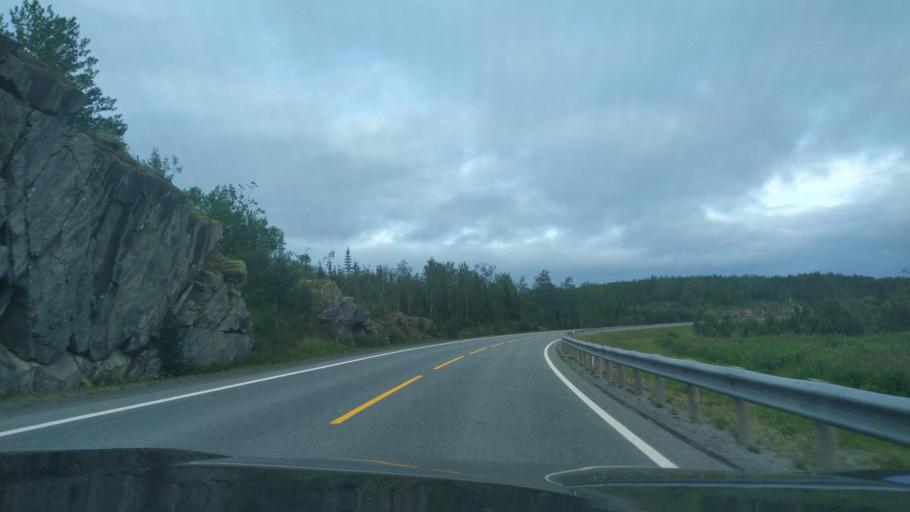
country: NO
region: Nordland
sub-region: Narvik
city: Narvik
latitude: 68.5317
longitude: 17.4159
